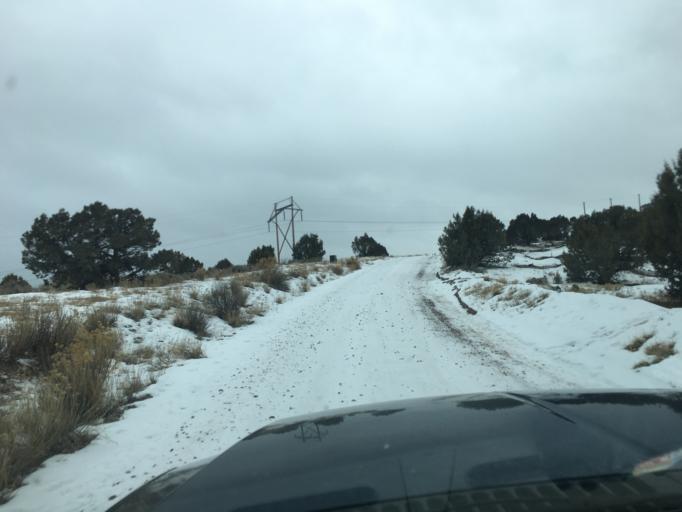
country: US
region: Colorado
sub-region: Garfield County
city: Parachute
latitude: 39.3461
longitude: -108.1690
